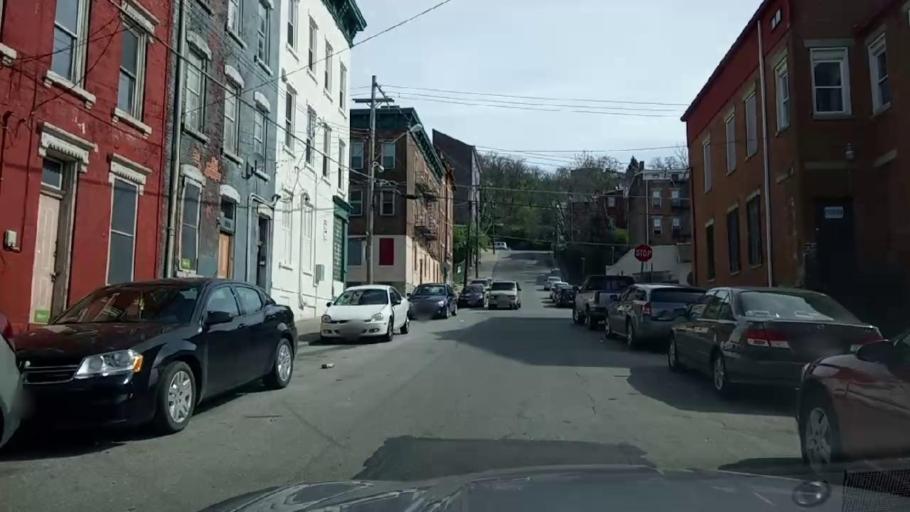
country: US
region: Kentucky
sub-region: Campbell County
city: Newport
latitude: 39.1151
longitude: -84.5141
